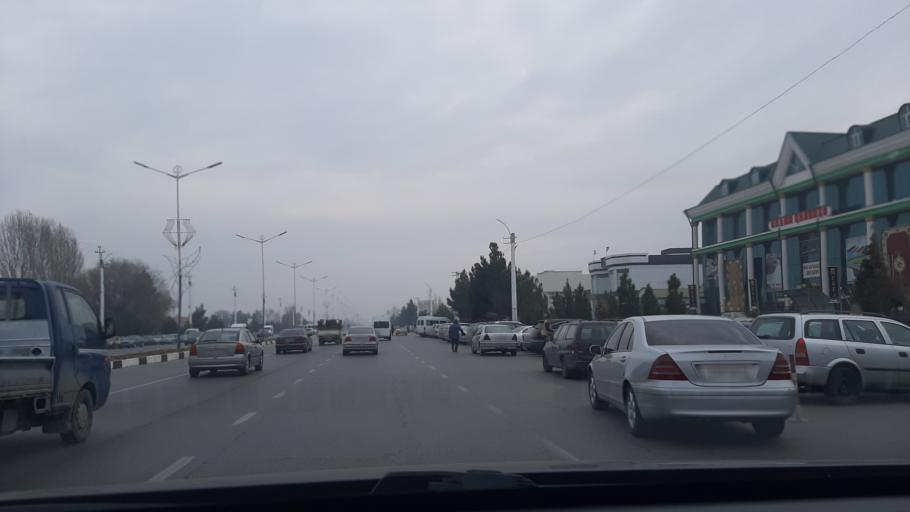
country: TJ
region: Viloyati Sughd
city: Chkalov
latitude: 40.2432
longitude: 69.7029
